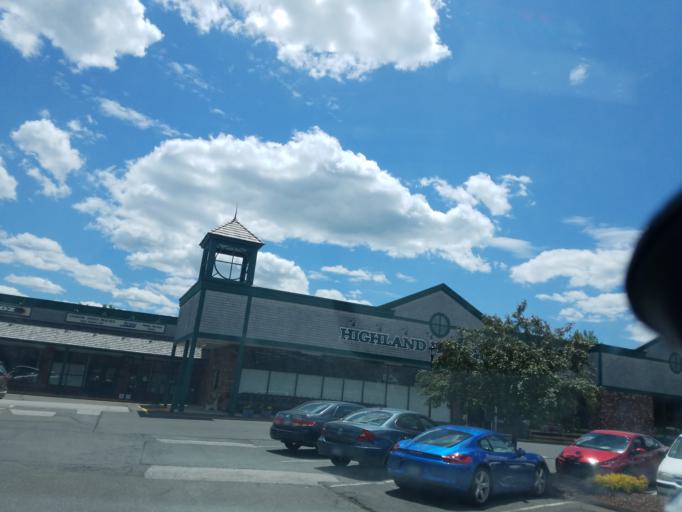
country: US
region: Connecticut
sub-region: Tolland County
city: Coventry Lake
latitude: 41.7978
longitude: -72.3741
